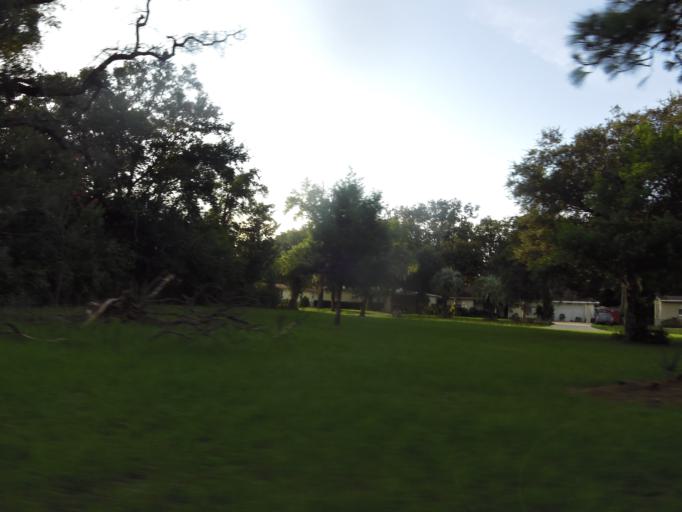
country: US
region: Florida
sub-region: Clay County
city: Orange Park
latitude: 30.2185
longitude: -81.7056
